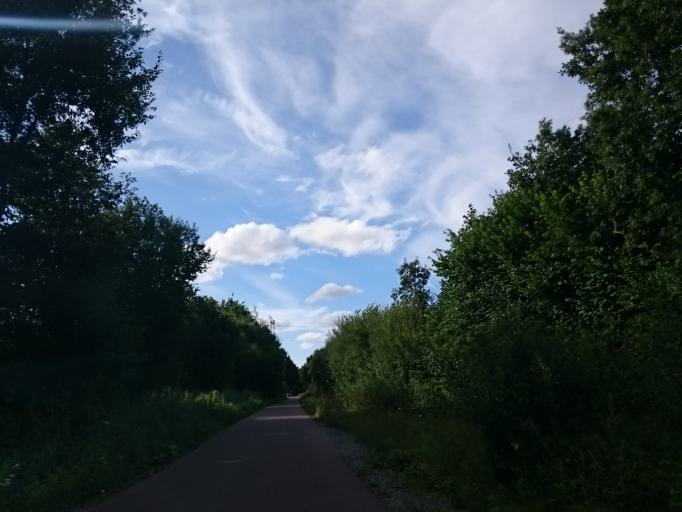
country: FR
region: Lower Normandy
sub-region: Departement du Calvados
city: Saint-Andre-sur-Orne
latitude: 49.1240
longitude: -0.4003
